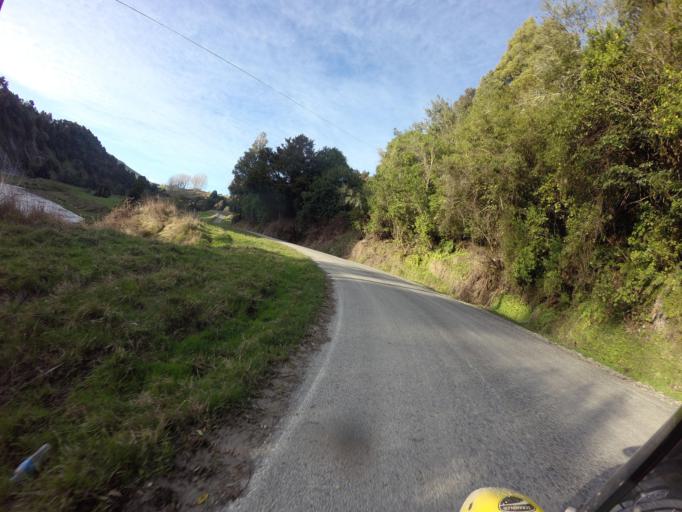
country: NZ
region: Hawke's Bay
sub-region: Wairoa District
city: Wairoa
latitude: -38.7346
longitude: 177.5892
